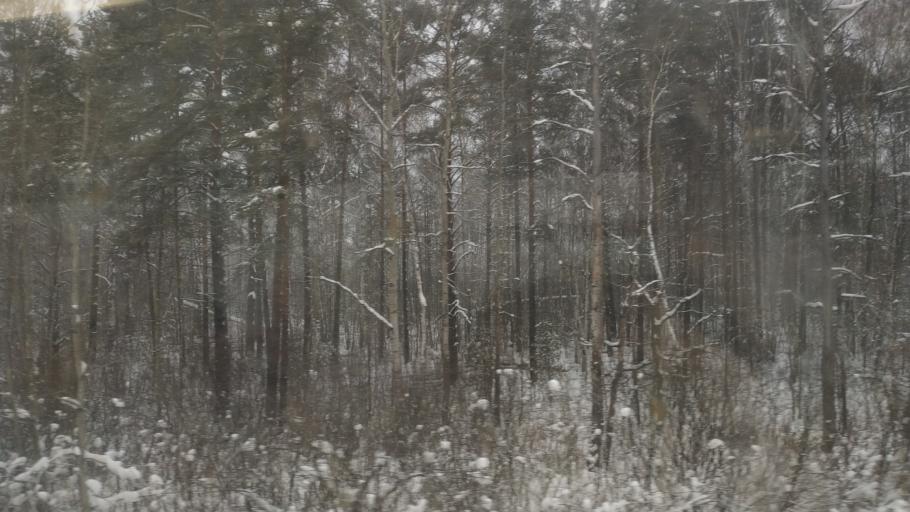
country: RU
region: Moskovskaya
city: Malyshevo
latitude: 55.5170
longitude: 38.3343
